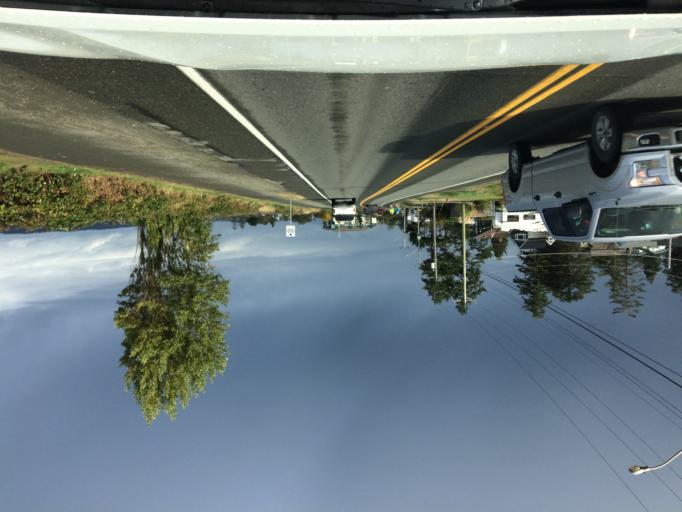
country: CA
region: British Columbia
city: Campbell River
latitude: 49.9589
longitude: -125.2074
